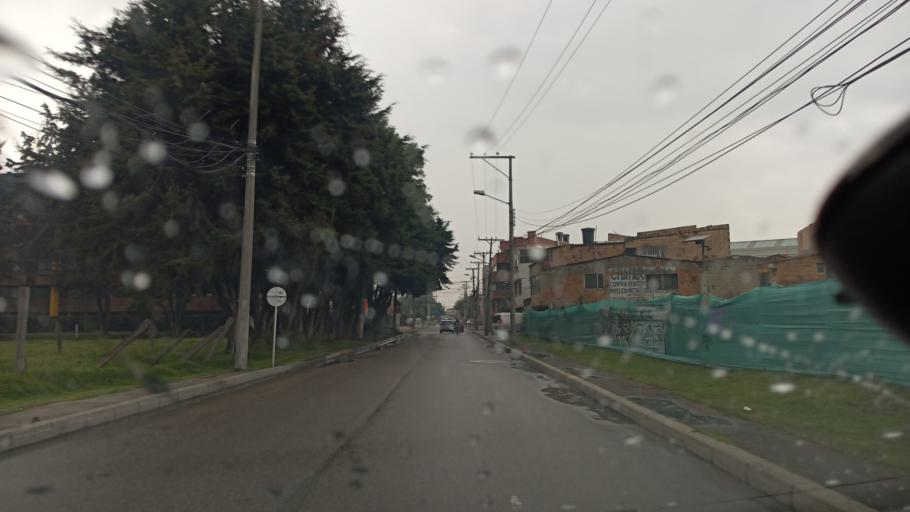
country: CO
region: Bogota D.C.
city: Bogota
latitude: 4.6809
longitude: -74.1277
